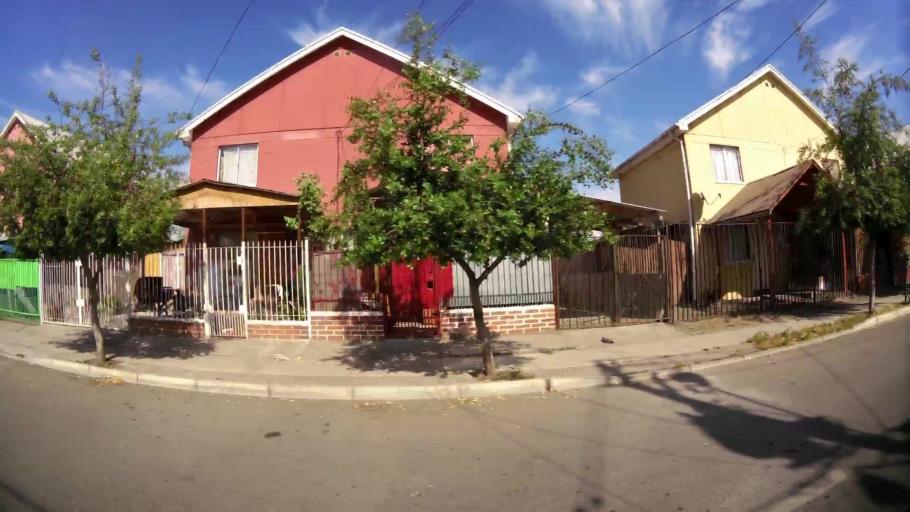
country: CL
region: Santiago Metropolitan
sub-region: Provincia de Talagante
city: El Monte
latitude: -33.6807
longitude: -70.9548
